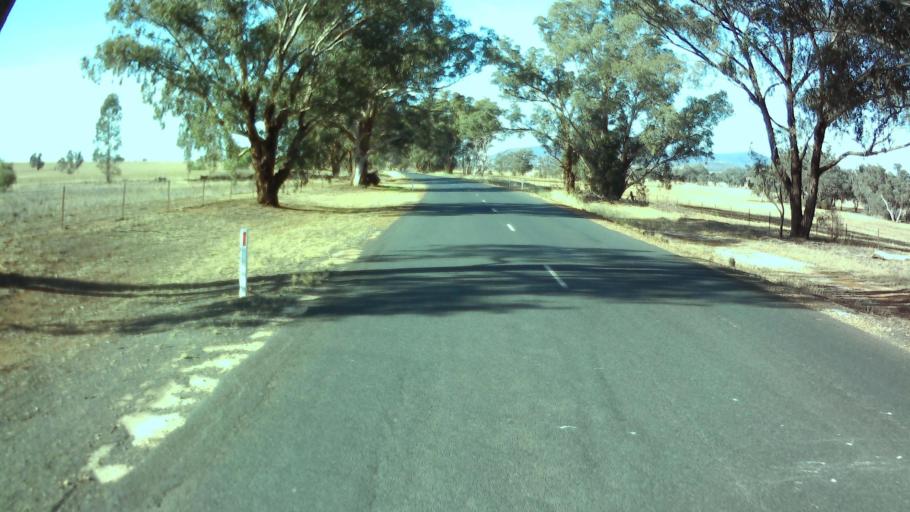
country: AU
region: New South Wales
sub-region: Weddin
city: Grenfell
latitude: -33.9148
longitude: 148.1428
